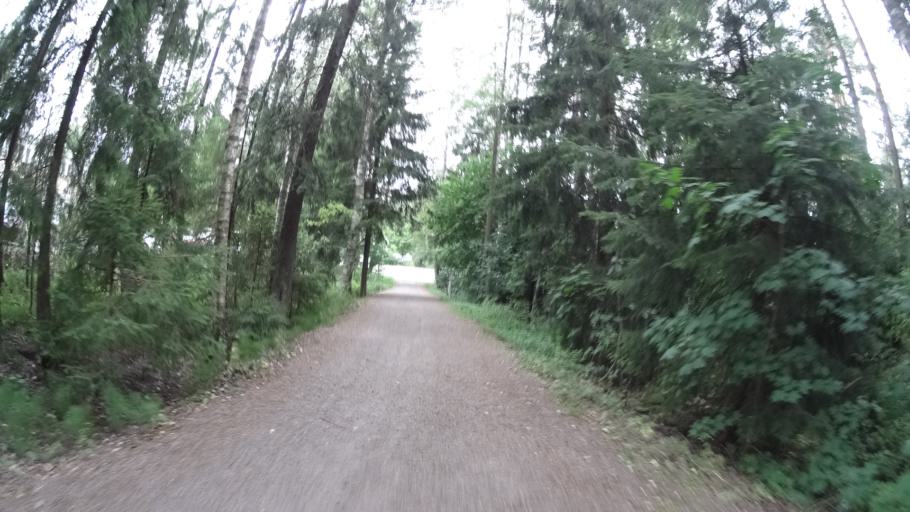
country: FI
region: Uusimaa
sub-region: Helsinki
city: Espoo
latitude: 60.1344
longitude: 24.6701
